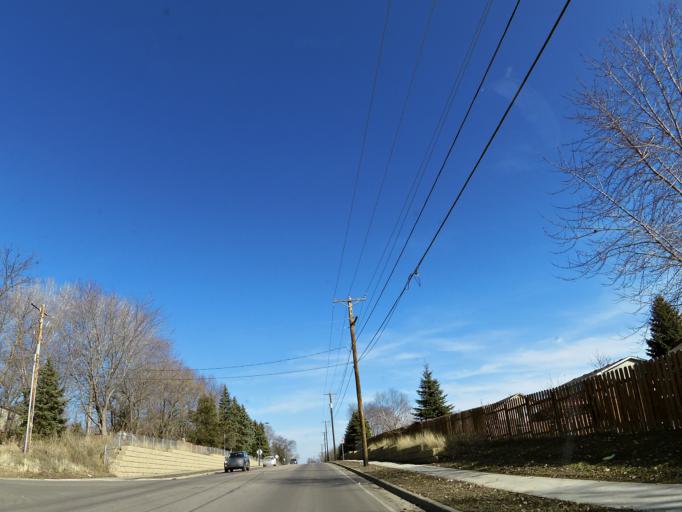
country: US
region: Minnesota
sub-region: Scott County
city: Prior Lake
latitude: 44.7029
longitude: -93.4529
